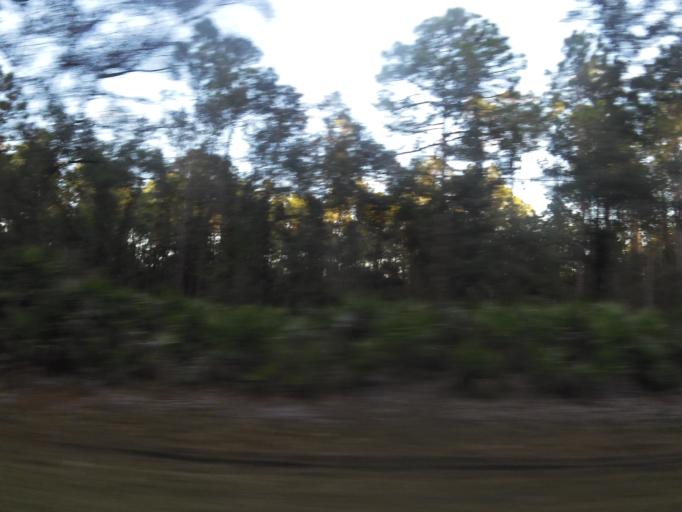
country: US
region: Florida
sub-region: Clay County
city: Green Cove Springs
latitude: 29.8846
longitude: -81.5612
